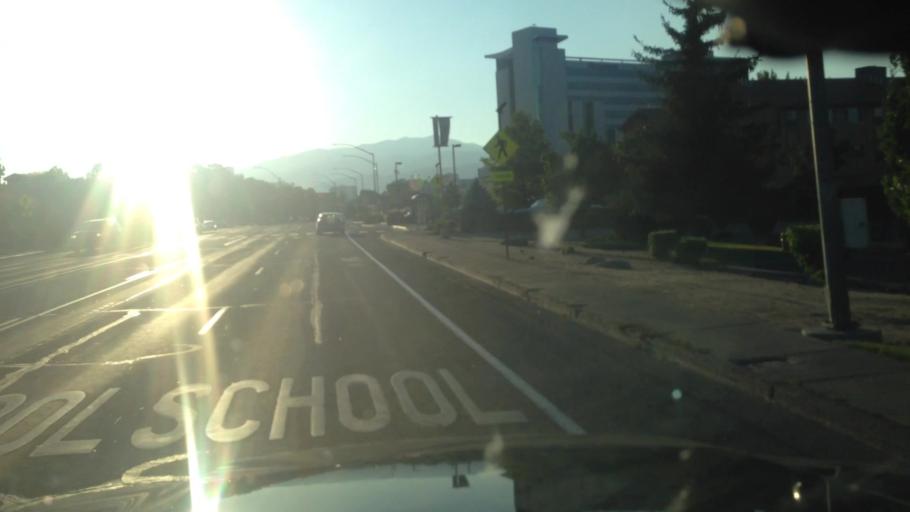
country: US
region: Nevada
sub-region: Washoe County
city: Reno
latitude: 39.5233
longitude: -119.7928
